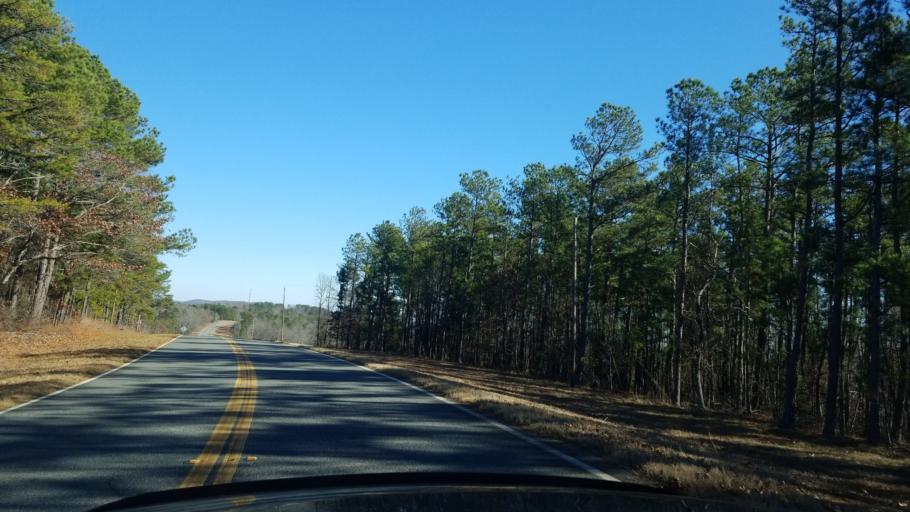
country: US
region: Georgia
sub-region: Meriwether County
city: Manchester
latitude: 32.8421
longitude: -84.6731
